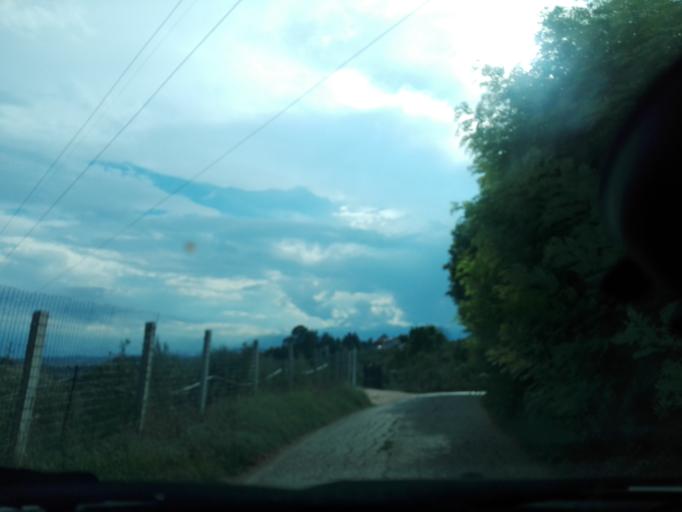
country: IT
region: Abruzzo
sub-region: Provincia di Pescara
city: Cappelle sul Tavo
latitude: 42.4581
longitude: 14.1044
